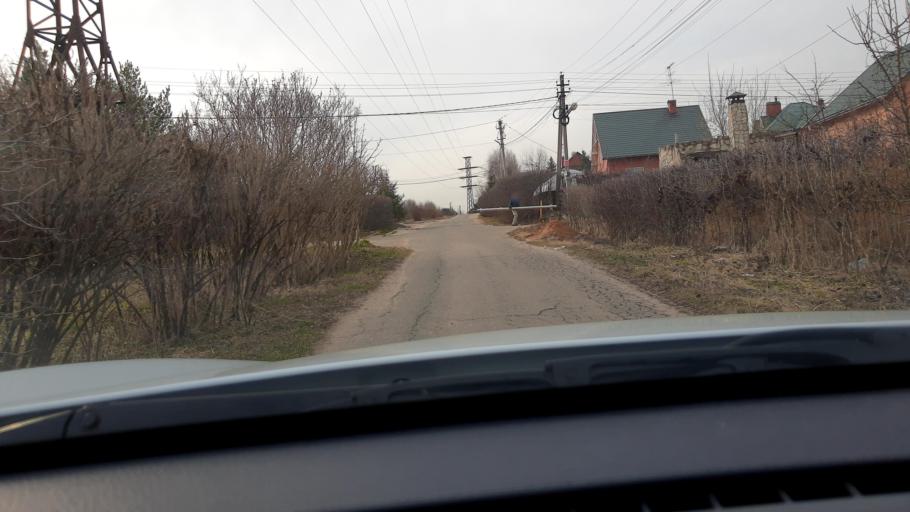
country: RU
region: Moskovskaya
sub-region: Leninskiy Rayon
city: Molokovo
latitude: 55.4924
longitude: 37.8524
